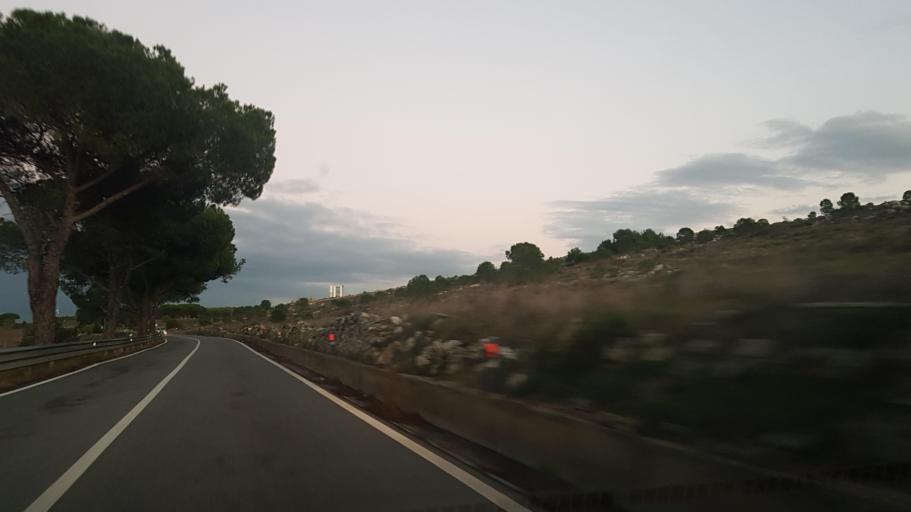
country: IT
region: Basilicate
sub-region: Provincia di Matera
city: Matera
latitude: 40.6769
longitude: 16.6334
